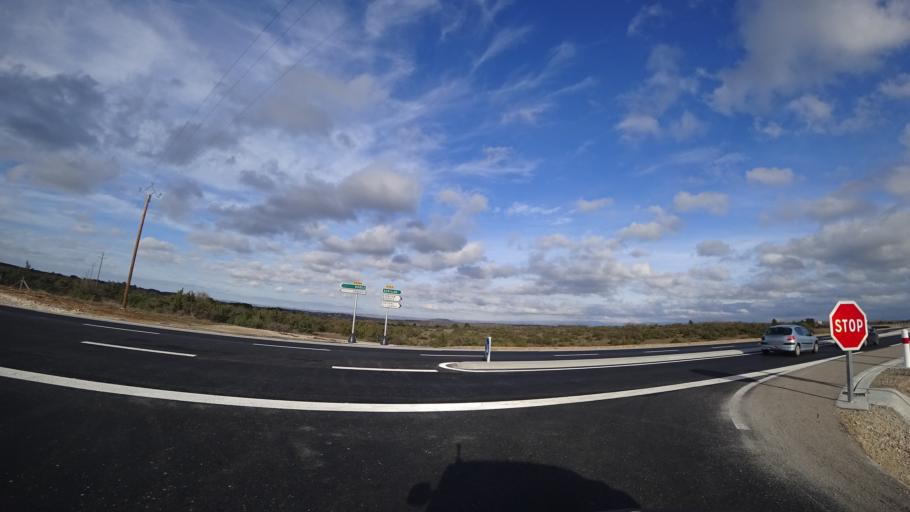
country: FR
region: Midi-Pyrenees
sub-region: Departement de l'Aveyron
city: La Loubiere
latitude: 44.4159
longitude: 2.6516
